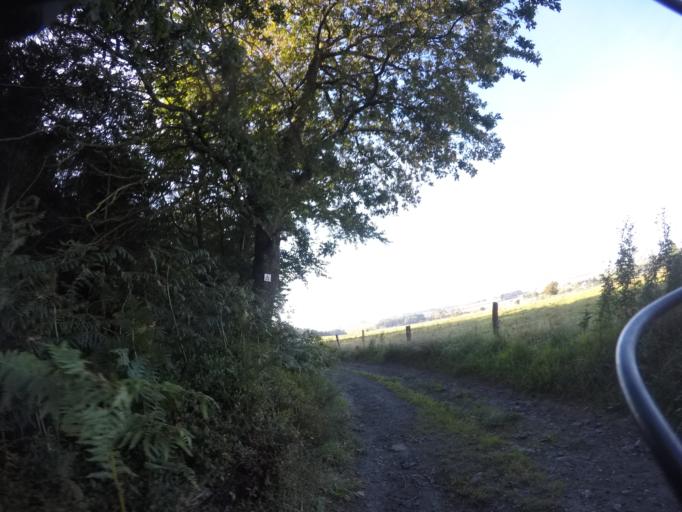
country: BE
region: Wallonia
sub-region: Province du Luxembourg
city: Bastogne
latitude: 49.9682
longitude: 5.6890
